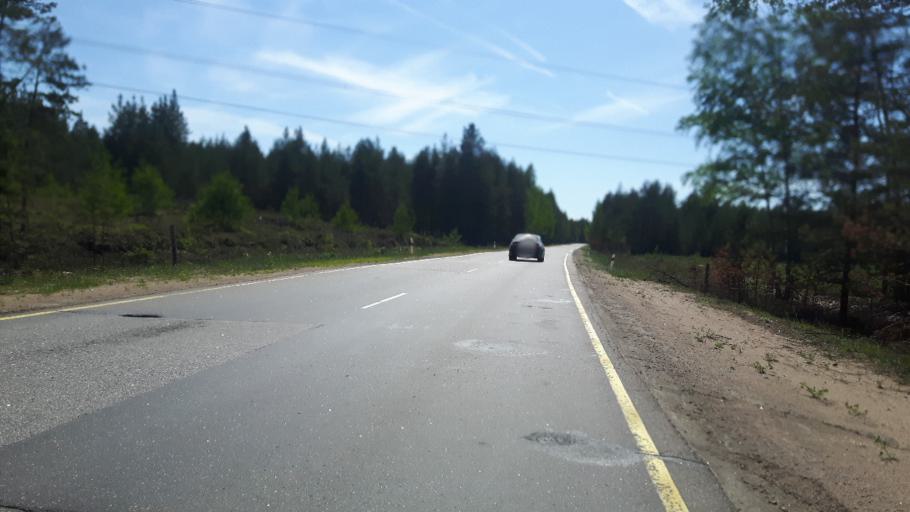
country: RU
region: Leningrad
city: Sista-Palkino
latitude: 59.7796
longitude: 28.8693
